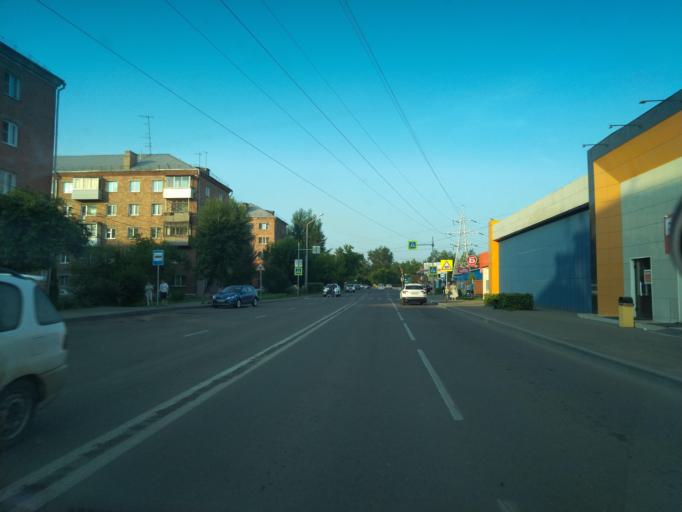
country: RU
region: Krasnoyarskiy
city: Krasnoyarsk
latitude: 56.0035
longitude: 92.9531
